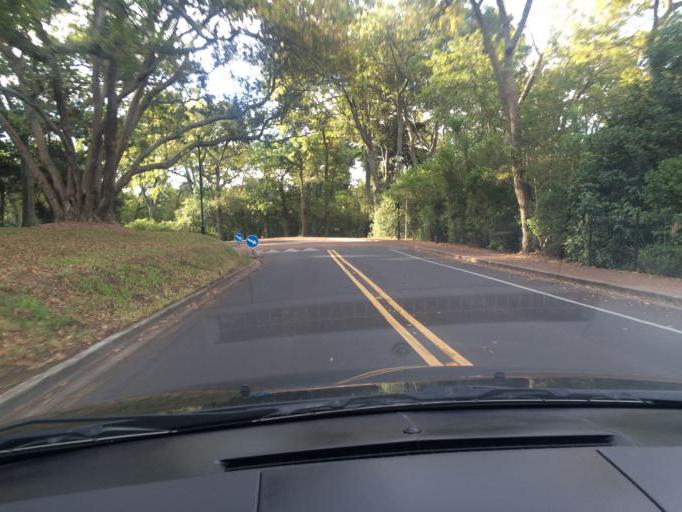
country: NZ
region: Auckland
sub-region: Auckland
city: Auckland
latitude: -36.8561
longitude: 174.7759
